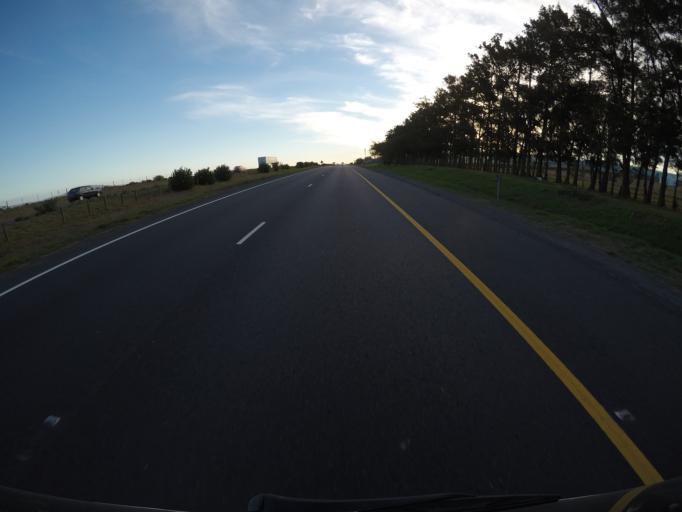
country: ZA
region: Western Cape
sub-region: City of Cape Town
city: Kraaifontein
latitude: -33.8091
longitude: 18.8296
